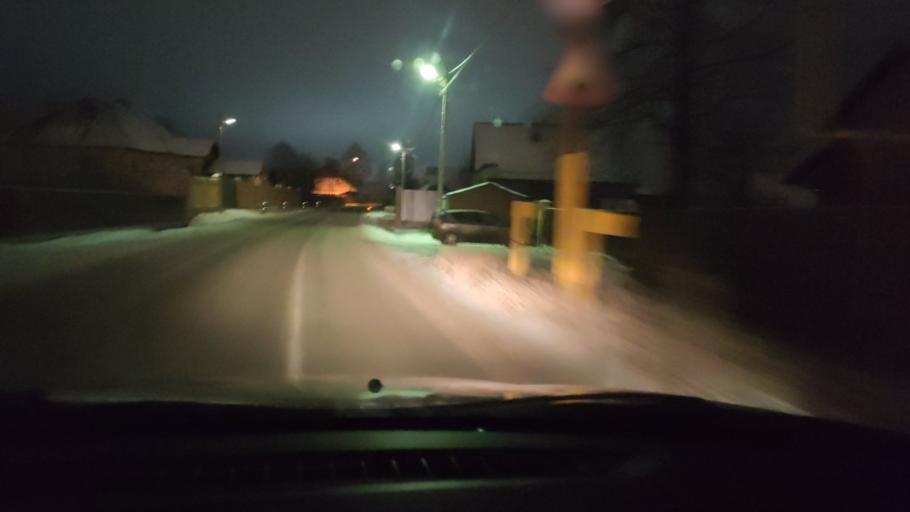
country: RU
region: Perm
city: Ferma
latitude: 57.9061
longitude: 56.3055
